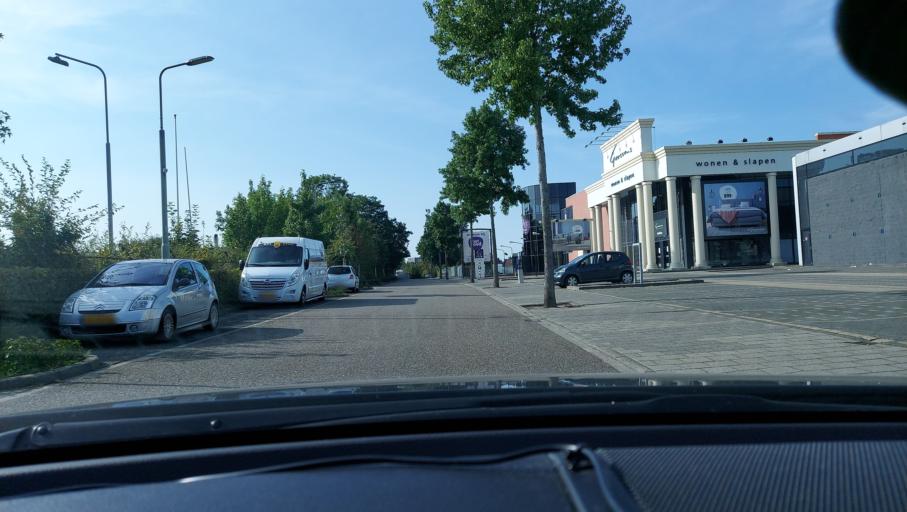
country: NL
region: Limburg
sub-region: Gemeente Roermond
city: Leeuwen
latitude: 51.2006
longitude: 6.0021
